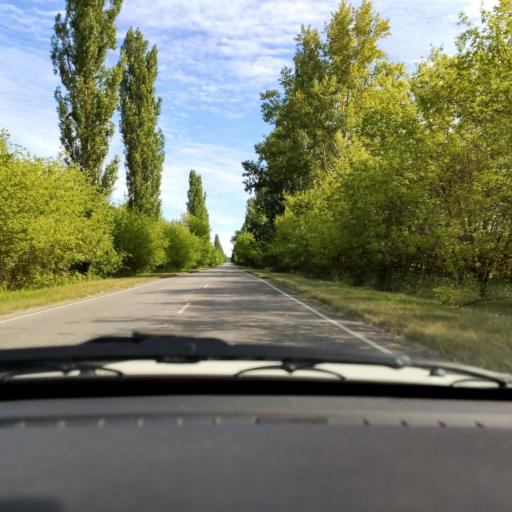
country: RU
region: Voronezj
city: Uglyanets
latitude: 51.8352
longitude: 39.6500
